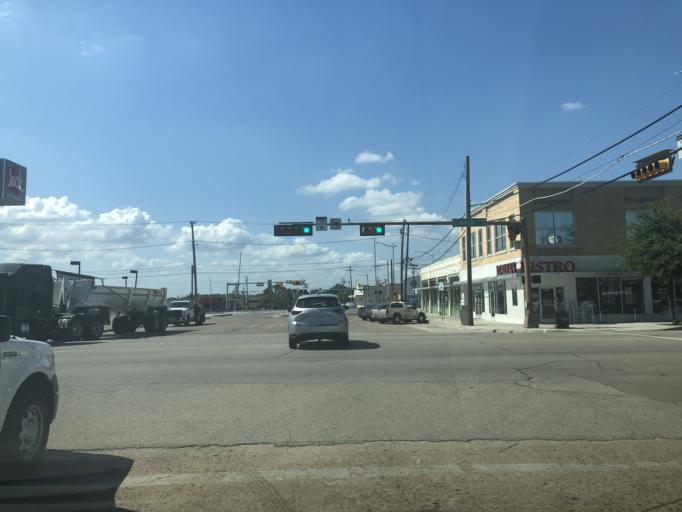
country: US
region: Texas
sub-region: Dallas County
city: Grand Prairie
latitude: 32.7456
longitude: -97.0036
